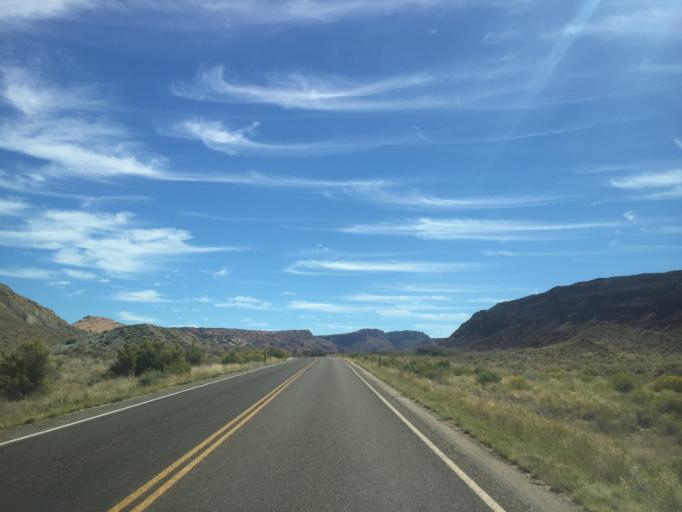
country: US
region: Utah
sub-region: Grand County
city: Moab
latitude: 38.7331
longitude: -109.5145
